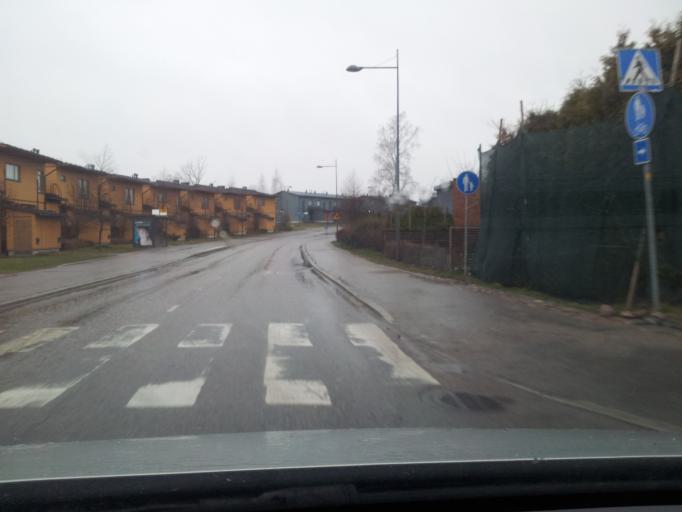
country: FI
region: Uusimaa
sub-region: Helsinki
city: Espoo
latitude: 60.1940
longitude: 24.5986
